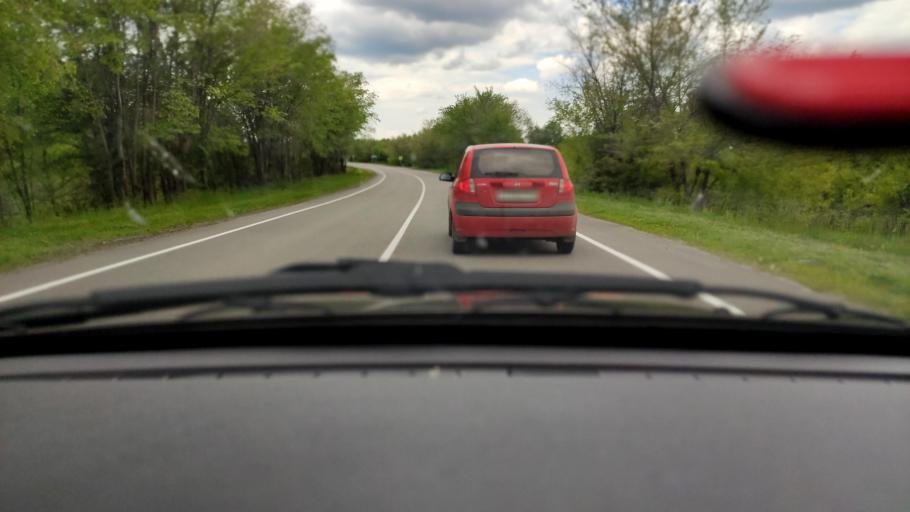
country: RU
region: Belgorod
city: Krasnoye
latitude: 51.0670
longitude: 38.8144
